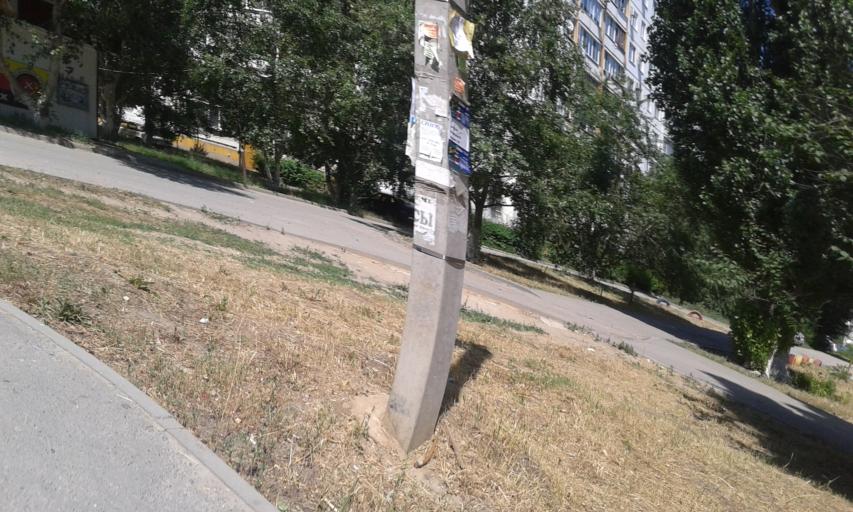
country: RU
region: Volgograd
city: Volgograd
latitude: 48.7537
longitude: 44.5074
